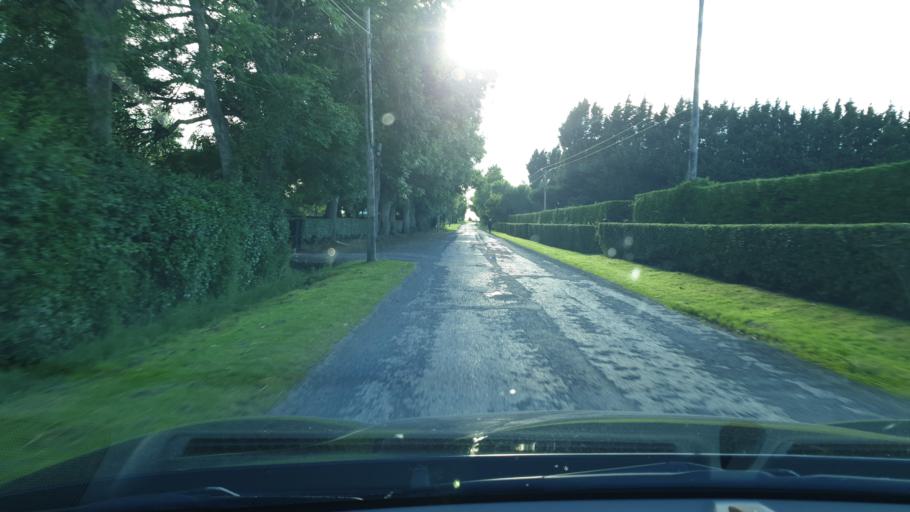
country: IE
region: Leinster
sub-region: Fingal County
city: Blanchardstown
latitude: 53.4373
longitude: -6.3887
